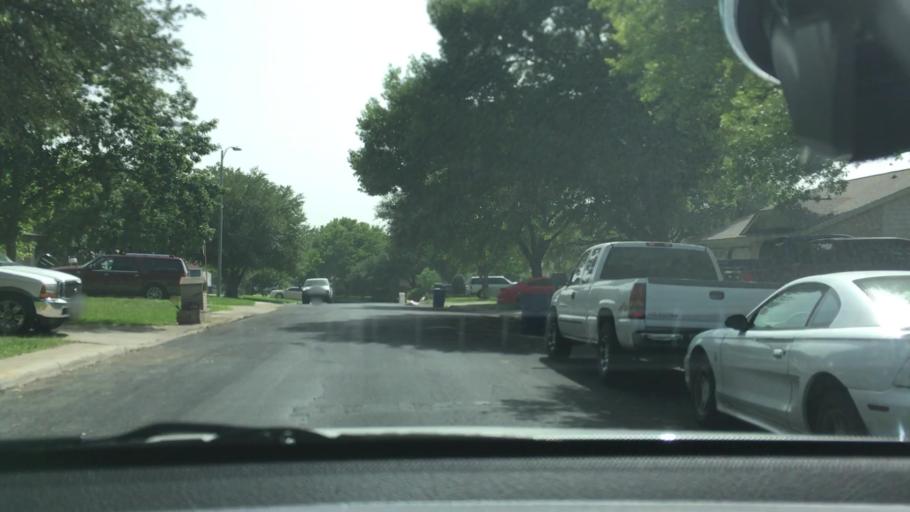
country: US
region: Texas
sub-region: Bexar County
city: Live Oak
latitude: 29.5933
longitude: -98.3792
